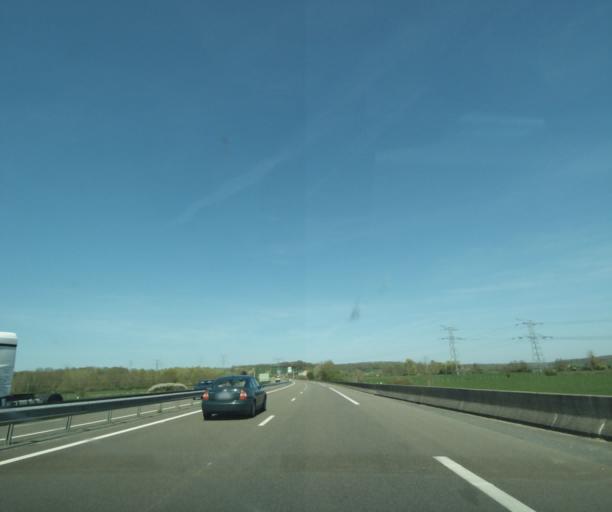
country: FR
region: Bourgogne
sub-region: Departement de la Nievre
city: Coulanges-les-Nevers
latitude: 47.0055
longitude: 3.2048
